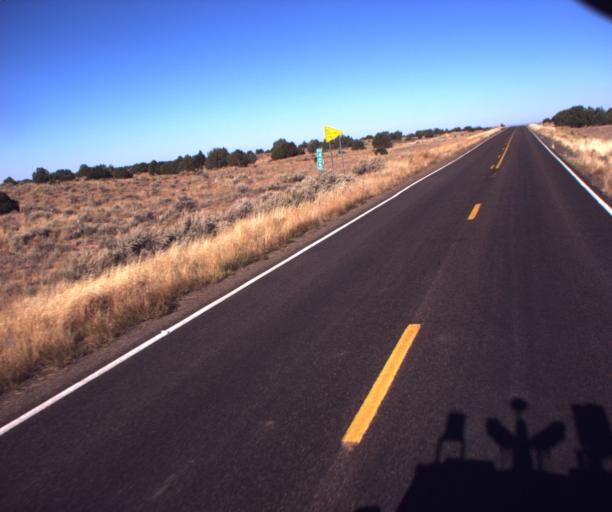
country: US
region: Arizona
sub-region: Navajo County
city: First Mesa
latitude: 35.7921
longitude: -110.1851
